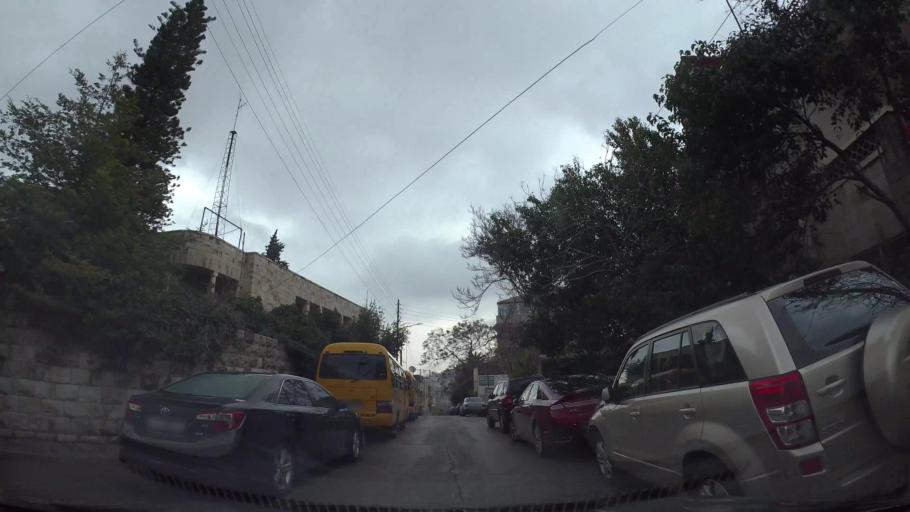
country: JO
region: Amman
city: Amman
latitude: 31.9485
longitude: 35.9301
